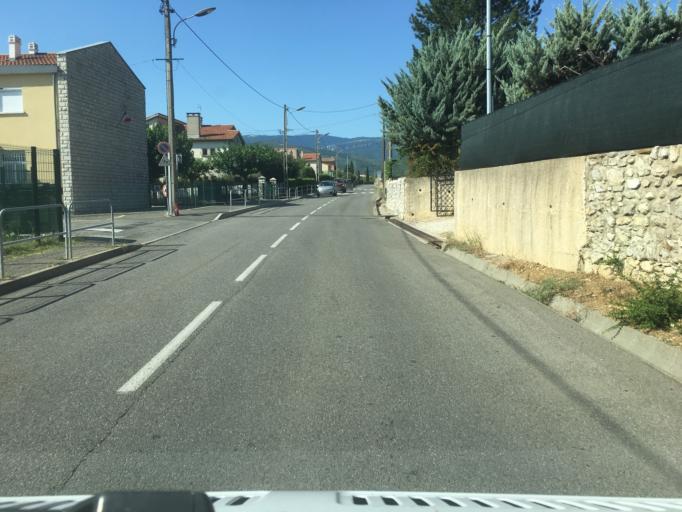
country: FR
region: Provence-Alpes-Cote d'Azur
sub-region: Departement des Alpes-de-Haute-Provence
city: Sisteron
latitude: 44.1853
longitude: 5.9386
